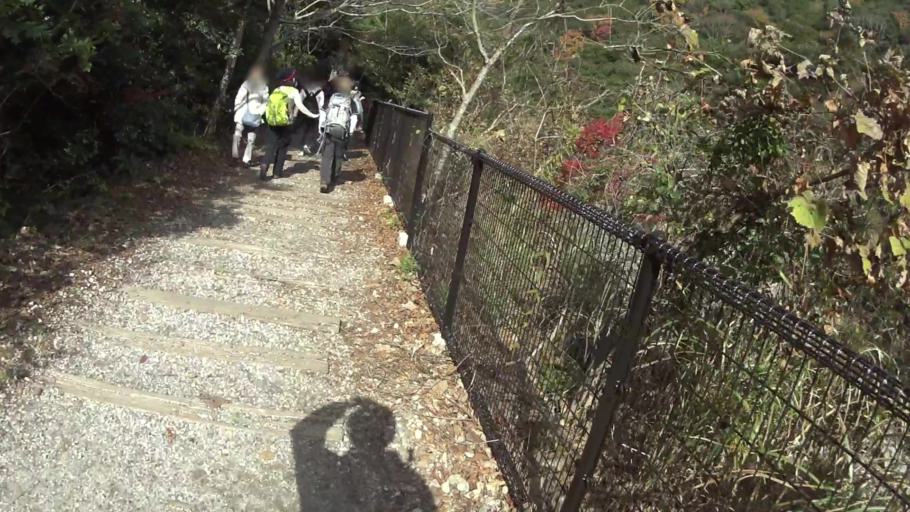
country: JP
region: Hyogo
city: Takarazuka
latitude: 34.8425
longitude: 135.3183
